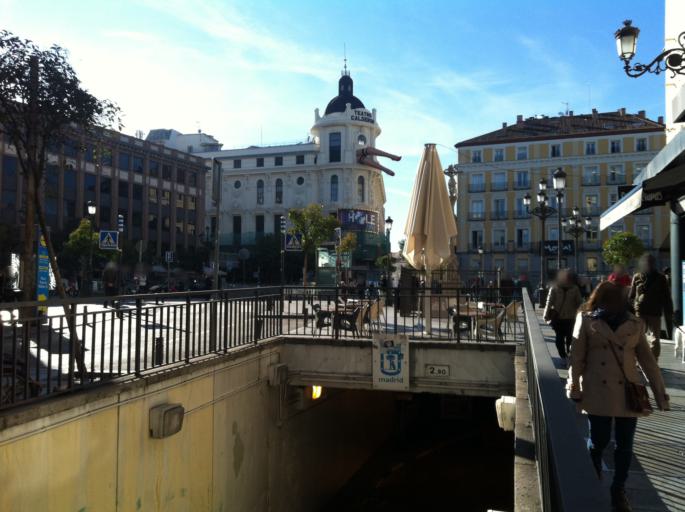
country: ES
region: Madrid
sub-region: Provincia de Madrid
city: Madrid
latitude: 40.4148
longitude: -3.7032
